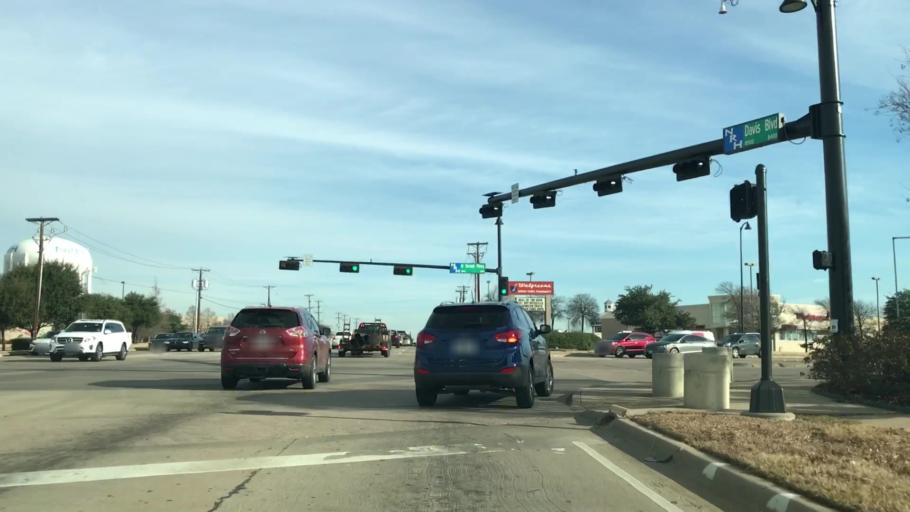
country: US
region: Texas
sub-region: Tarrant County
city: Colleyville
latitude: 32.9037
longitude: -97.1937
